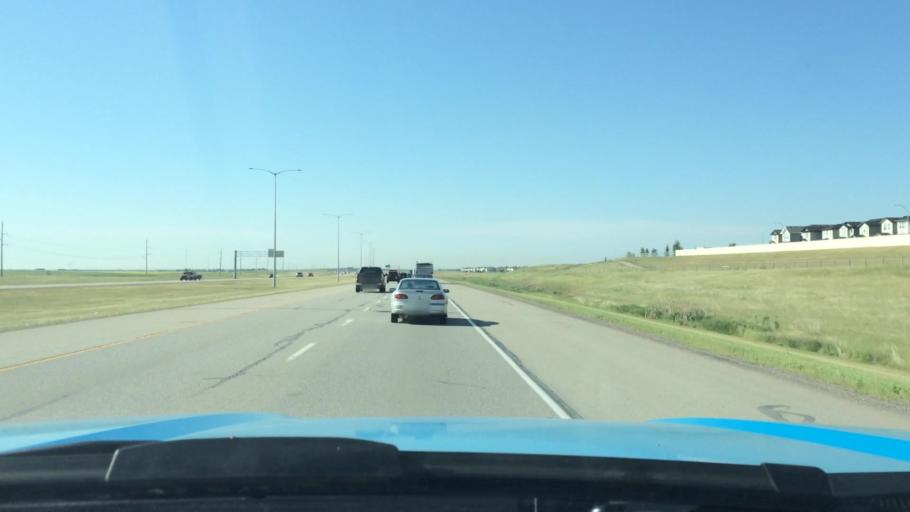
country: CA
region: Alberta
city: Chestermere
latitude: 51.1214
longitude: -113.9216
